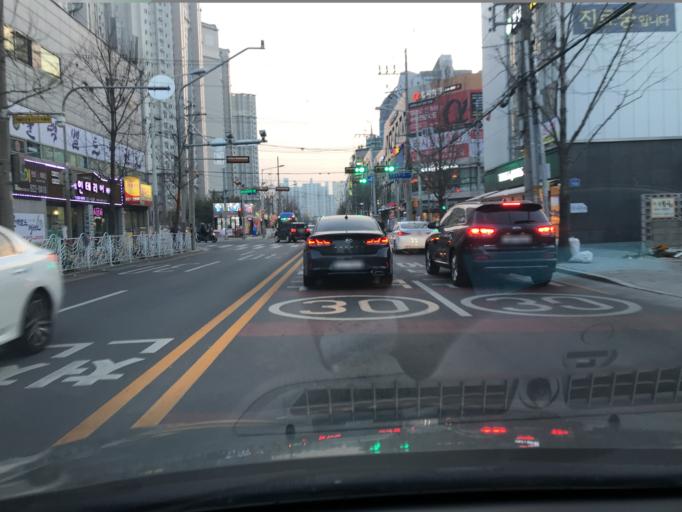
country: KR
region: Daegu
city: Hwawon
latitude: 35.8172
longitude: 128.5182
